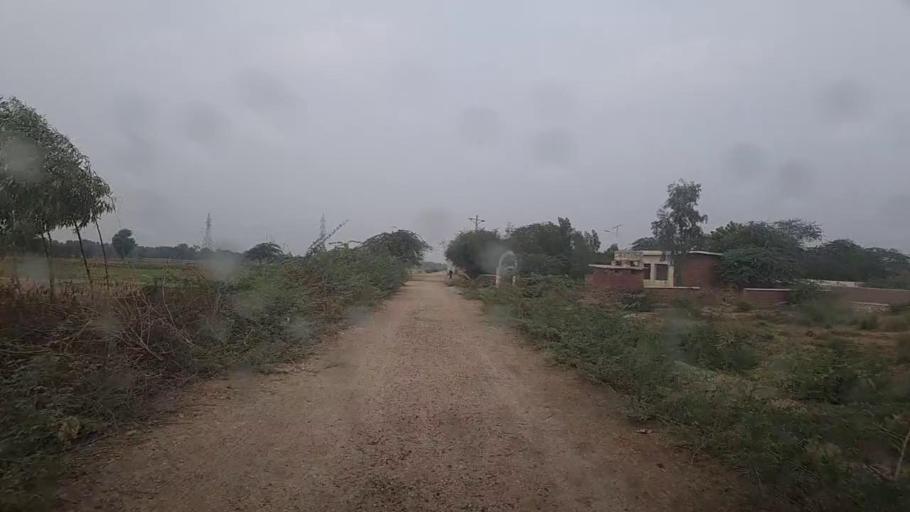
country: PK
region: Sindh
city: Gambat
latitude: 27.3650
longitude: 68.5873
